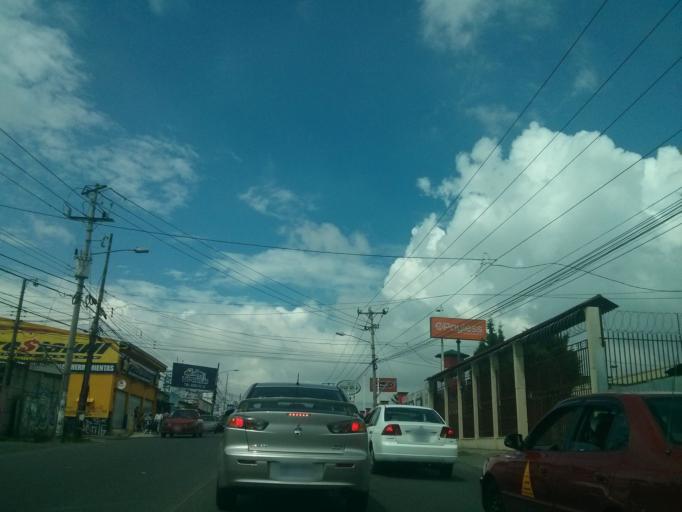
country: CR
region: San Jose
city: San Rafael Arriba
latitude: 9.8902
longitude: -84.0644
